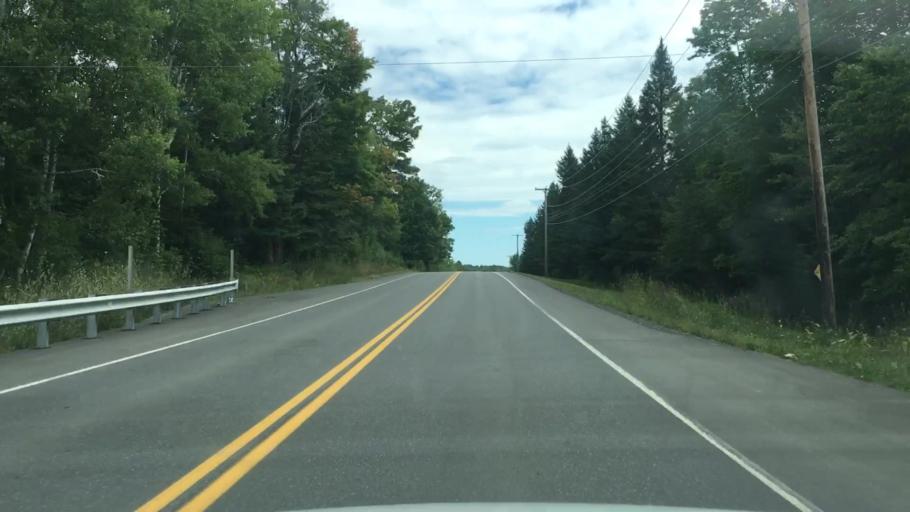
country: US
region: Maine
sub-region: Piscataquis County
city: Milo
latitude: 45.2409
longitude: -69.0414
